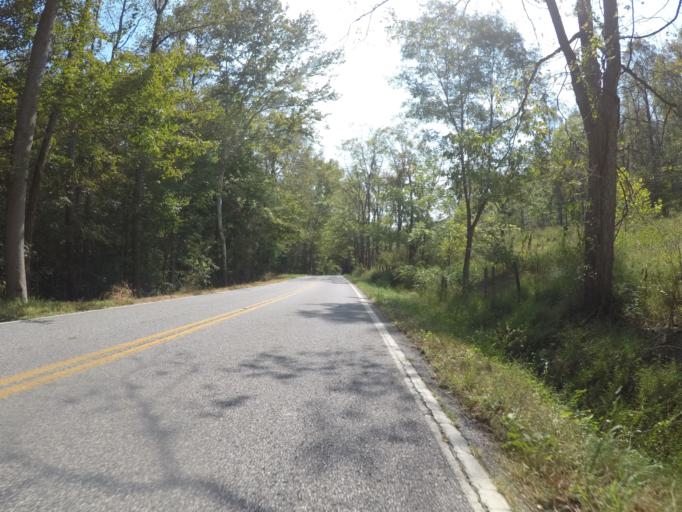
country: US
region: West Virginia
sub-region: Cabell County
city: Lesage
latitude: 38.5831
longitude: -82.4208
